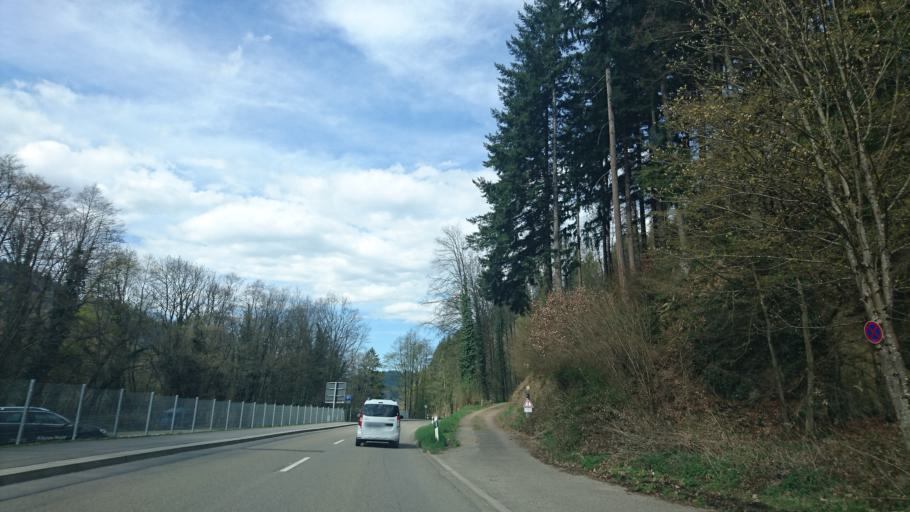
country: DE
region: Baden-Wuerttemberg
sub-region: Freiburg Region
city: Horben
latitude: 47.9412
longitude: 7.8678
